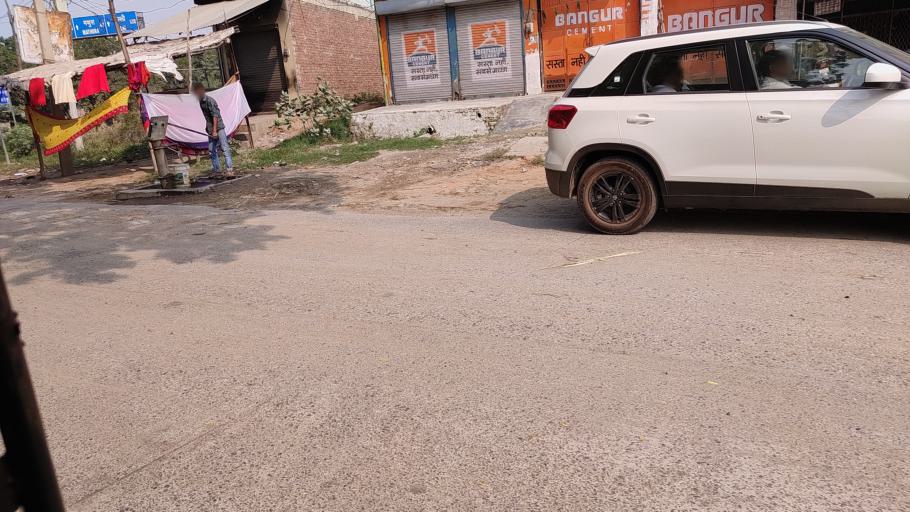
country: IN
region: Uttar Pradesh
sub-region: Mathura
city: Barsana
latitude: 27.6578
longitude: 77.3823
